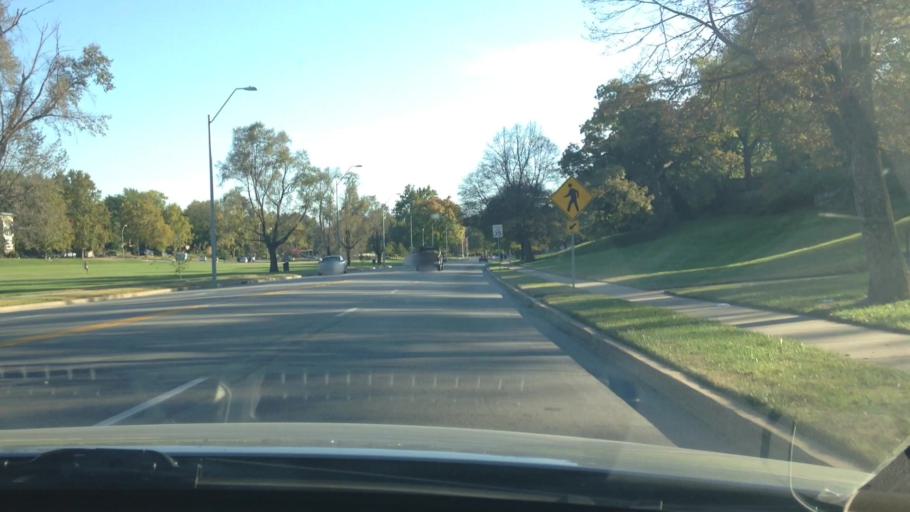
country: US
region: Kansas
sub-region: Johnson County
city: Westwood
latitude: 39.0551
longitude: -94.5796
